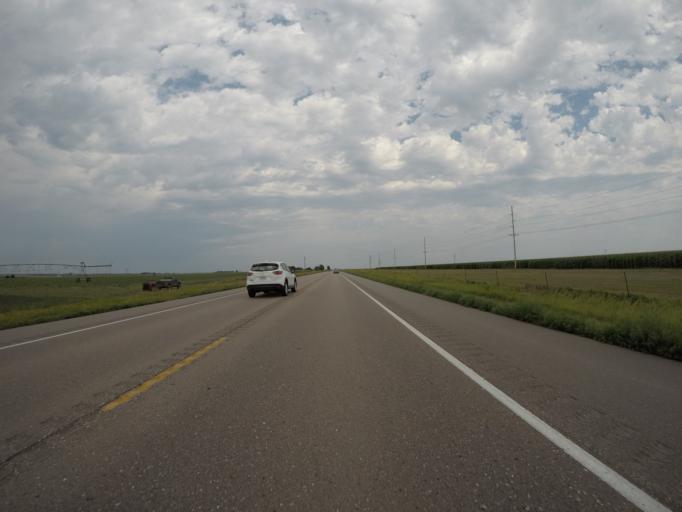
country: US
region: Nebraska
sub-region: Clay County
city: Harvard
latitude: 40.5828
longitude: -98.1334
